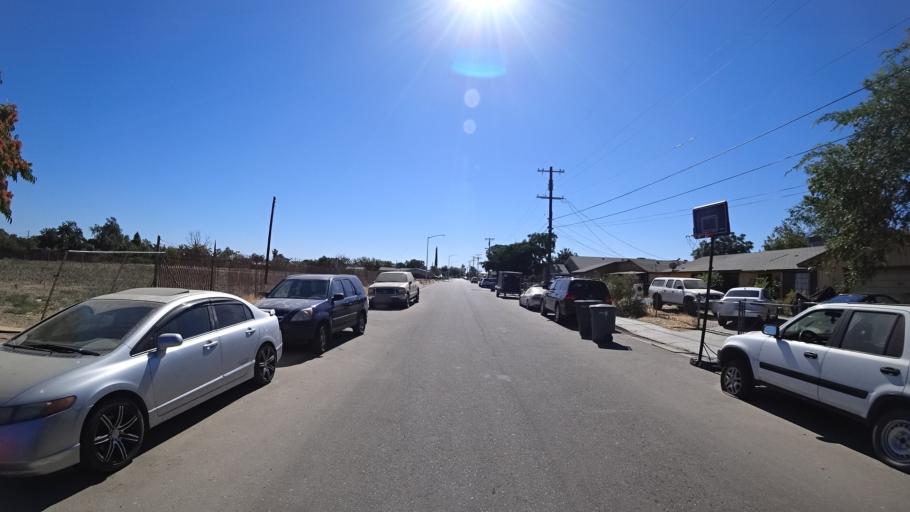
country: US
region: California
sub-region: Fresno County
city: Easton
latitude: 36.6909
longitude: -119.7986
